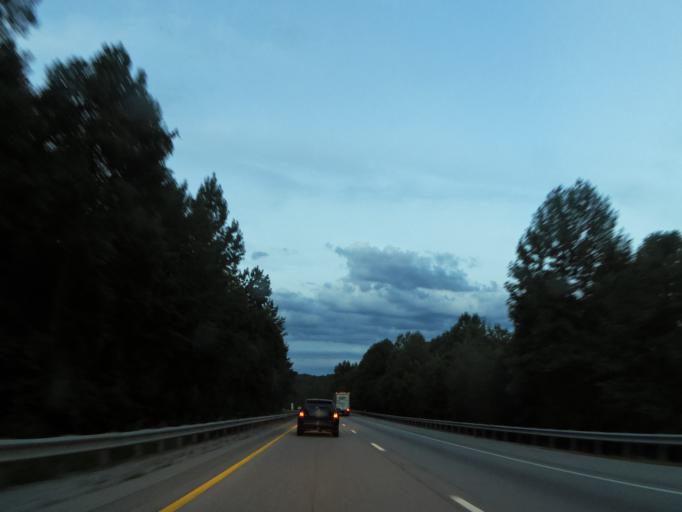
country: US
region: Tennessee
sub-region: Roane County
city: Rockwood
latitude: 35.8999
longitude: -84.6363
